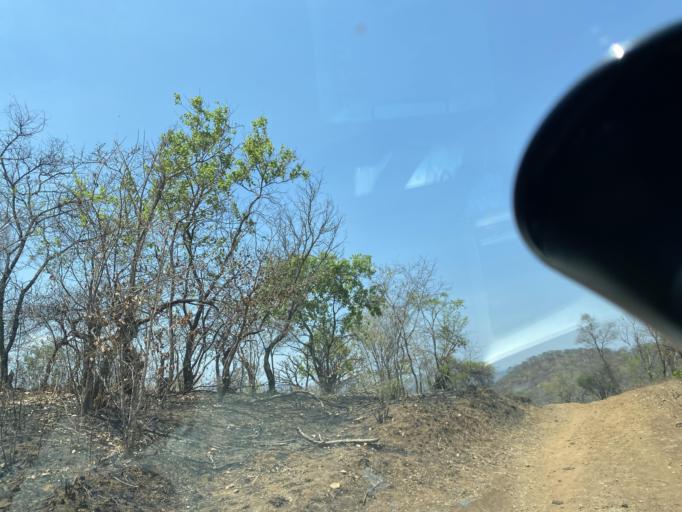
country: ZM
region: Lusaka
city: Kafue
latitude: -15.8004
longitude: 28.4529
